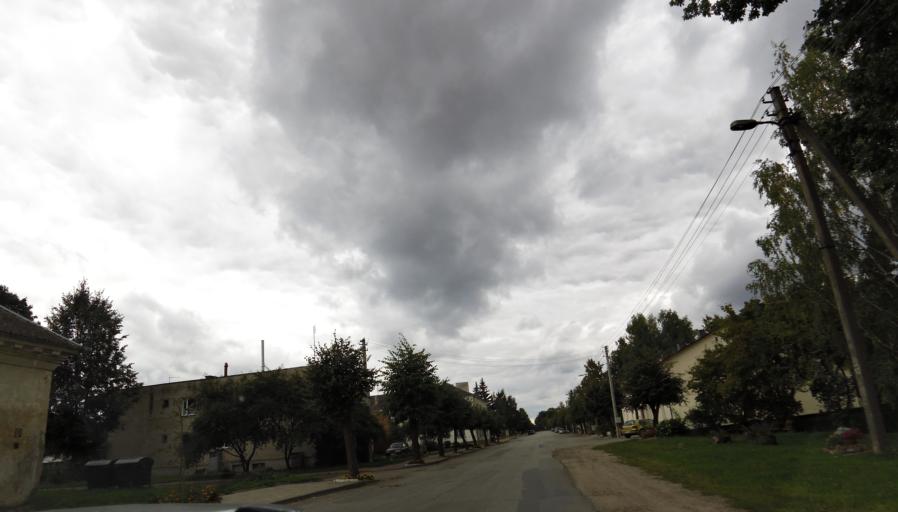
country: LT
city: Linkuva
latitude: 56.0253
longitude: 24.1686
